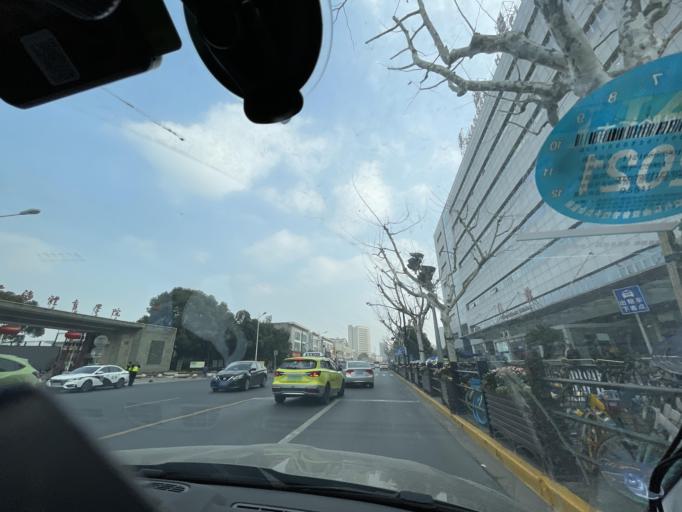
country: CN
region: Shanghai Shi
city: Yangpu
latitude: 31.3117
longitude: 121.5210
